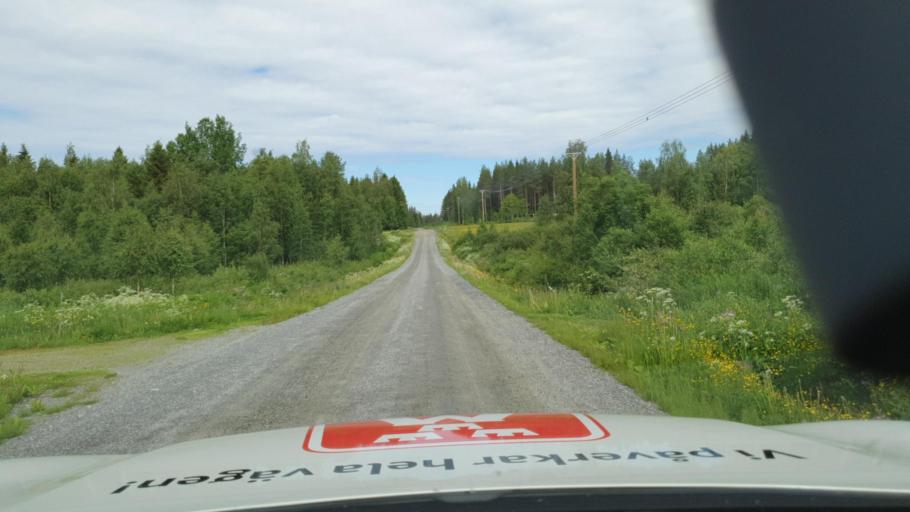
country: SE
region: Vaesterbotten
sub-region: Skelleftea Kommun
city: Langsele
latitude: 64.5729
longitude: 20.2990
